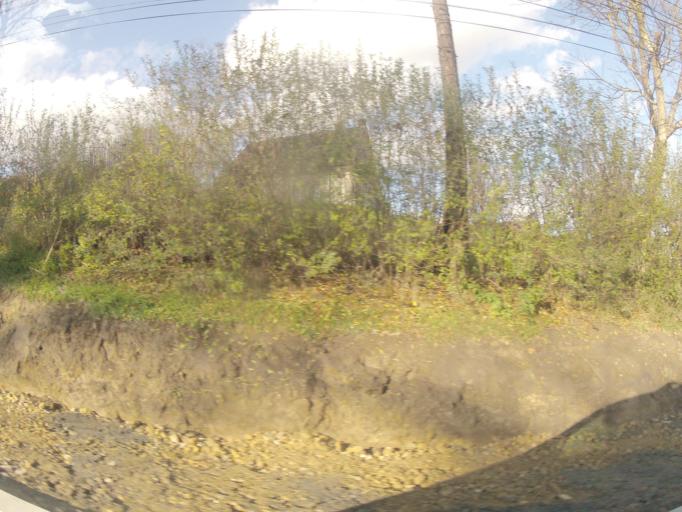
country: PL
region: Lesser Poland Voivodeship
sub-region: Powiat krakowski
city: Rzaska
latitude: 50.0681
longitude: 19.8319
